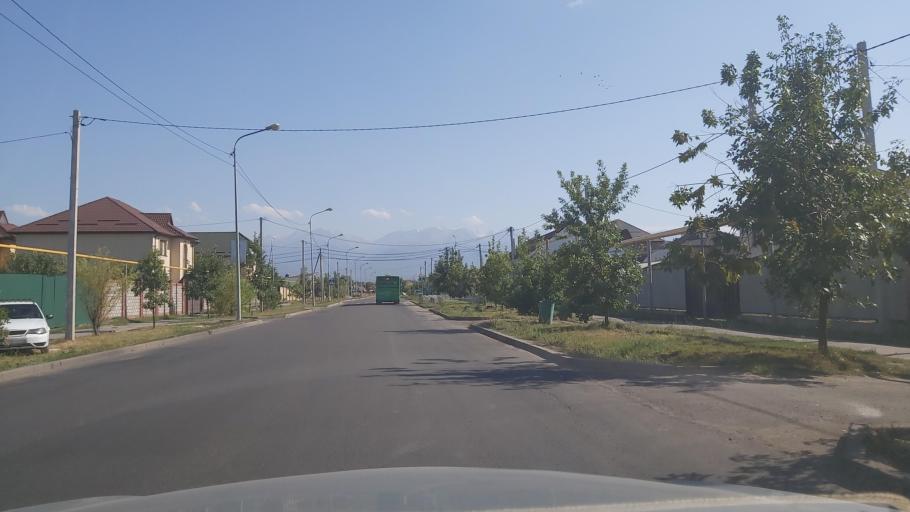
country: KZ
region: Almaty Oblysy
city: Burunday
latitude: 43.3167
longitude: 76.8420
